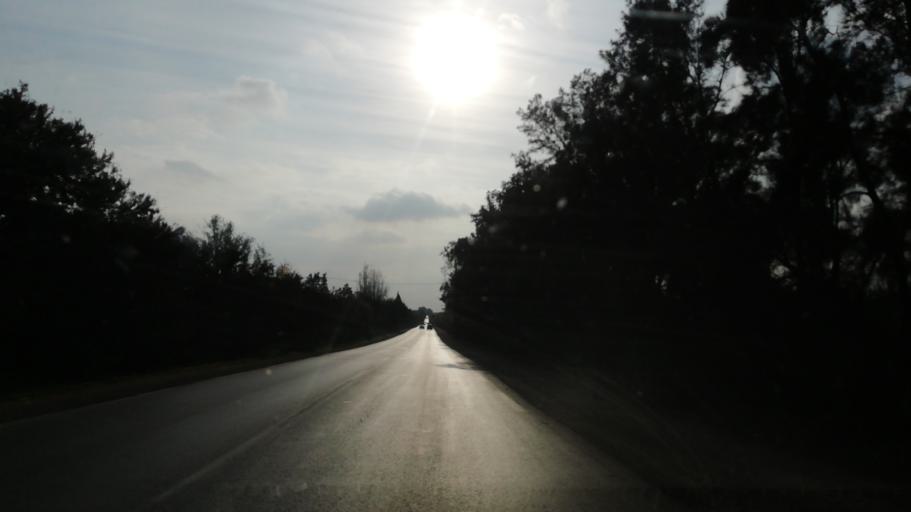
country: DZ
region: Mostaganem
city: Mostaganem
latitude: 35.8387
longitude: 0.0619
